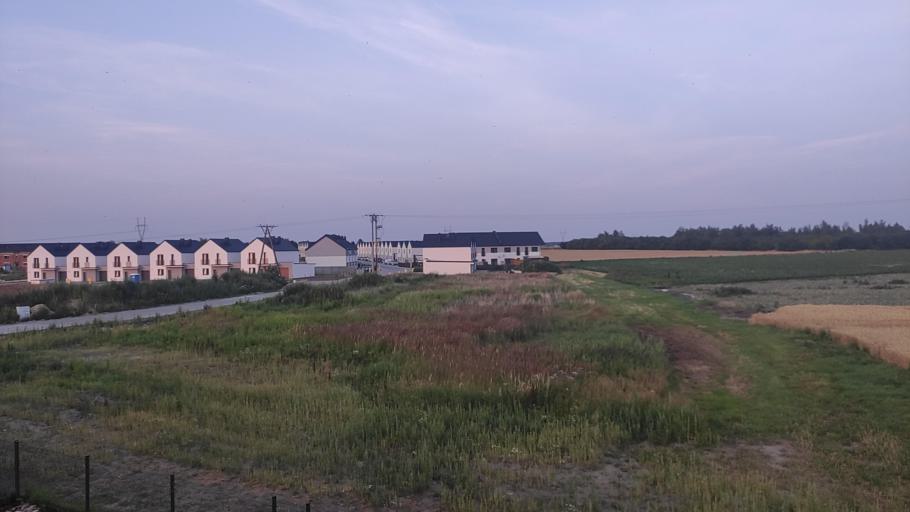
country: PL
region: Greater Poland Voivodeship
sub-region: Powiat poznanski
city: Kostrzyn
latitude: 52.4071
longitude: 17.2118
